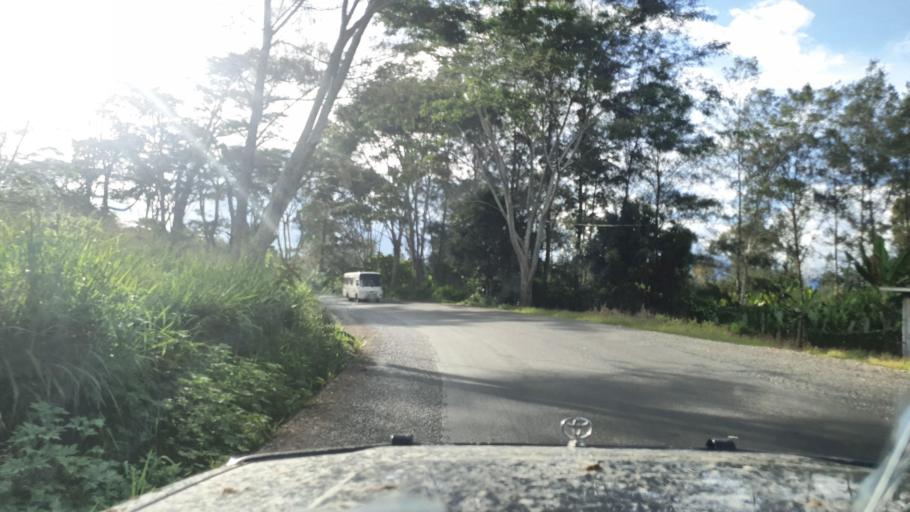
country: PG
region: Jiwaka
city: Minj
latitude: -5.8420
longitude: 144.6212
